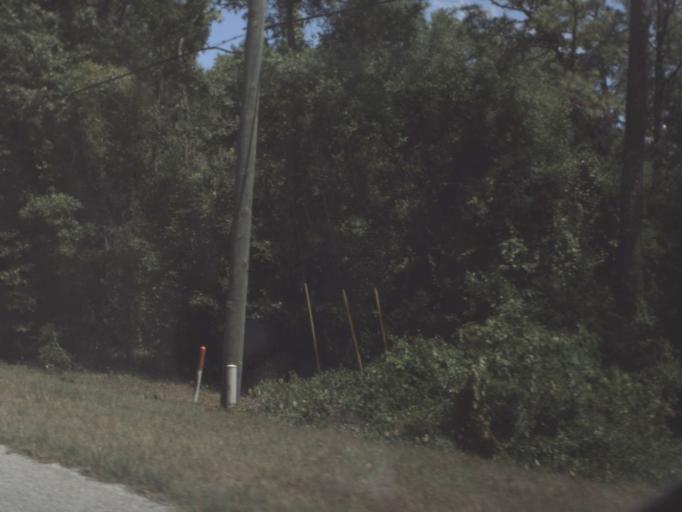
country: US
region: Florida
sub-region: Marion County
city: Silver Springs Shores
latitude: 29.1987
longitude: -81.9171
